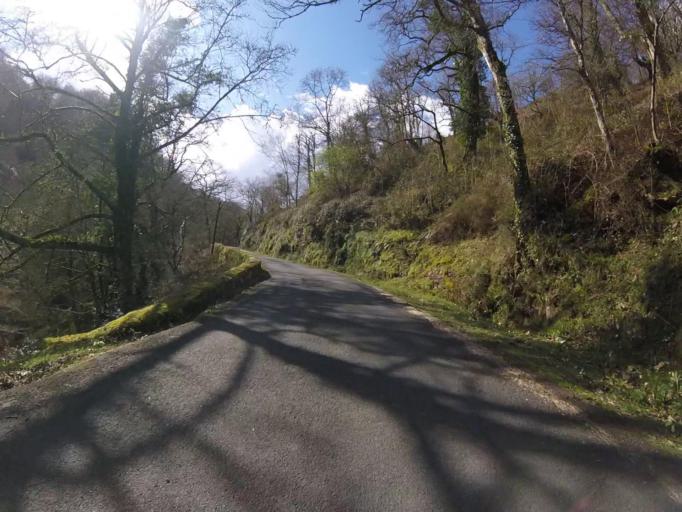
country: ES
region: Navarre
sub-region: Provincia de Navarra
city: Etxalar
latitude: 43.2657
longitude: -1.6049
